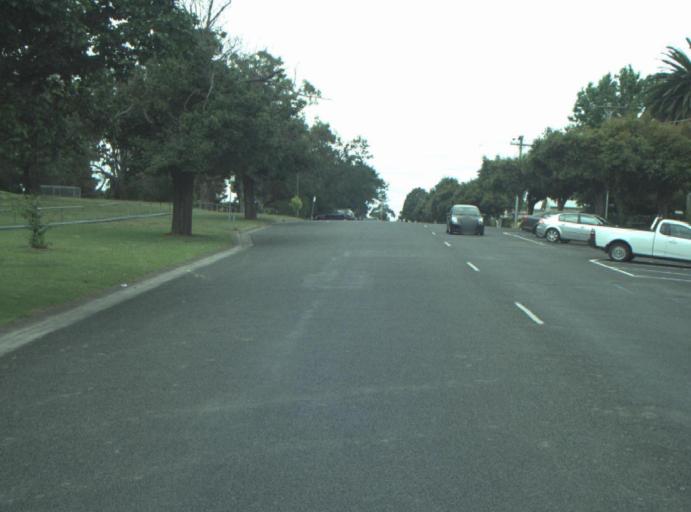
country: AU
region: Victoria
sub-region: Greater Geelong
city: East Geelong
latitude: -38.1488
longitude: 144.3741
